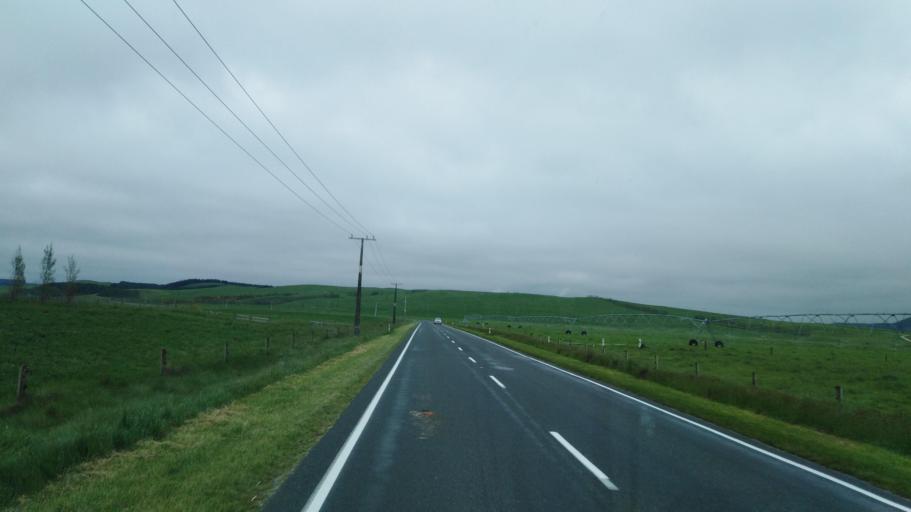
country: NZ
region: Waikato
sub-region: Taupo District
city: Taupo
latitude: -38.6164
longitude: 176.2367
